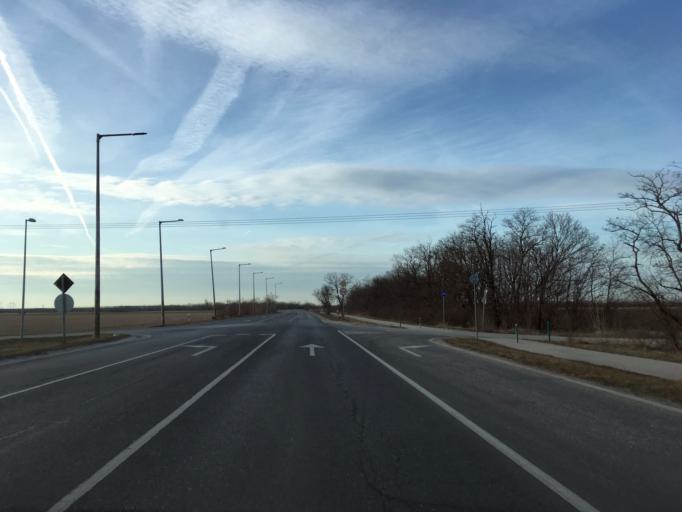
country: HU
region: Gyor-Moson-Sopron
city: Mosonmagyarovar
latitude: 47.9017
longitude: 17.1987
